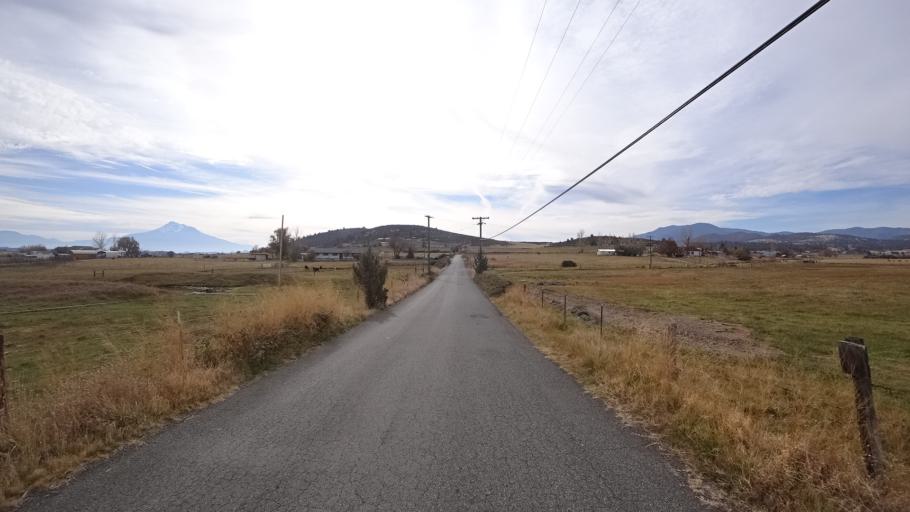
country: US
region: California
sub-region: Siskiyou County
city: Montague
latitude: 41.7012
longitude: -122.5495
